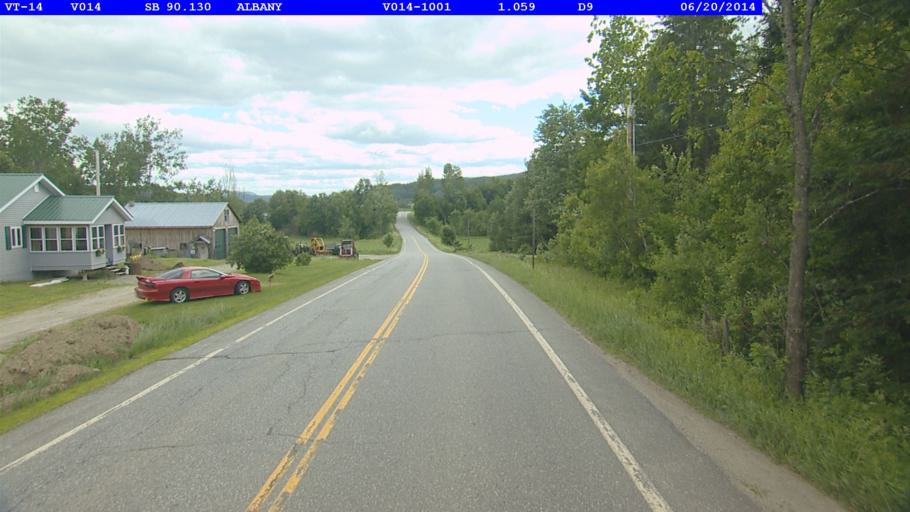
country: US
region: Vermont
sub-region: Caledonia County
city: Hardwick
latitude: 44.7173
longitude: -72.3857
